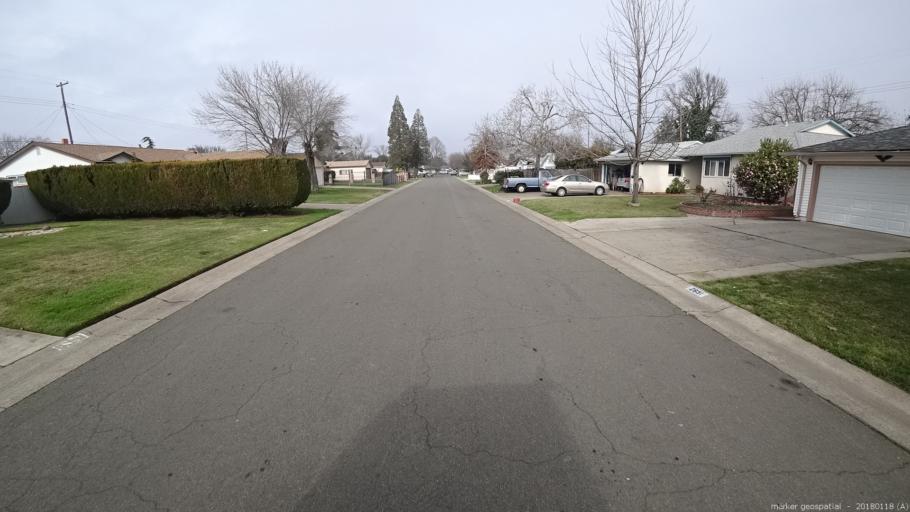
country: US
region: California
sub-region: Sacramento County
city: Rancho Cordova
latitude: 38.5917
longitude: -121.3069
